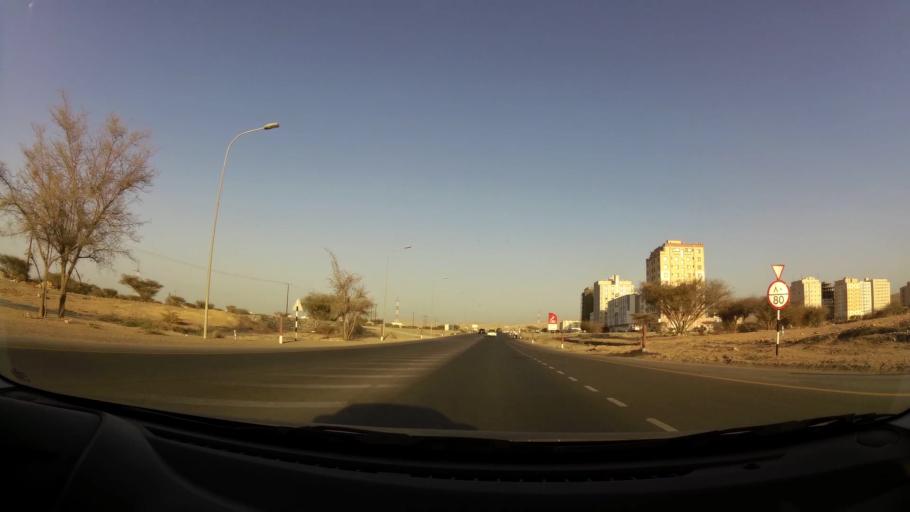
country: OM
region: Muhafazat Masqat
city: As Sib al Jadidah
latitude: 23.5779
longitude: 58.1793
